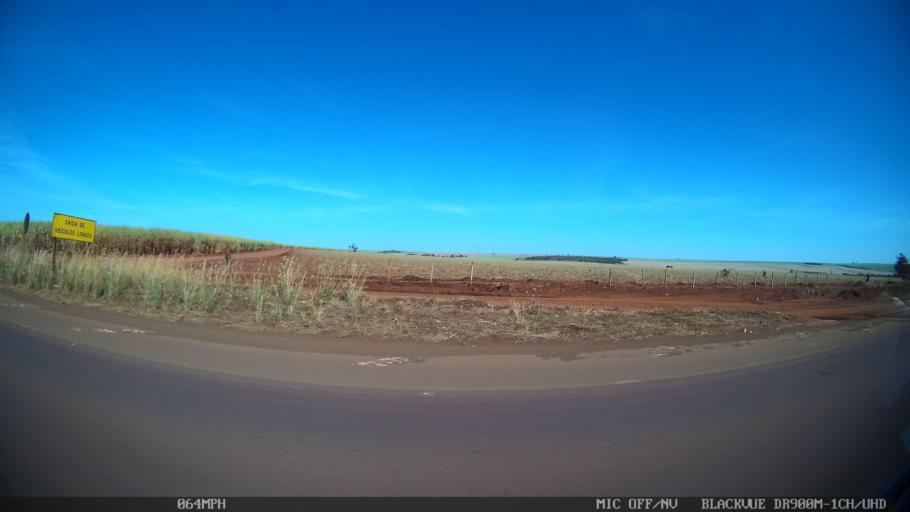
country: BR
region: Sao Paulo
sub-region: Ipua
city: Ipua
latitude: -20.4963
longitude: -47.9718
